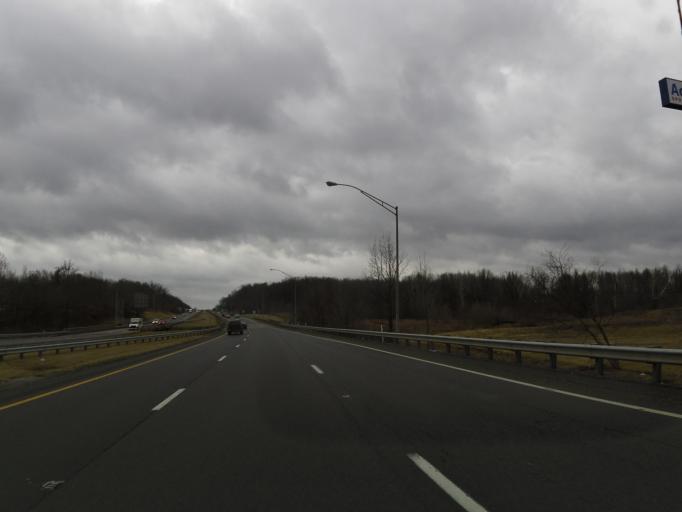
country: US
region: Kentucky
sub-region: McCracken County
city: Hendron
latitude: 37.0762
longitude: -88.6795
